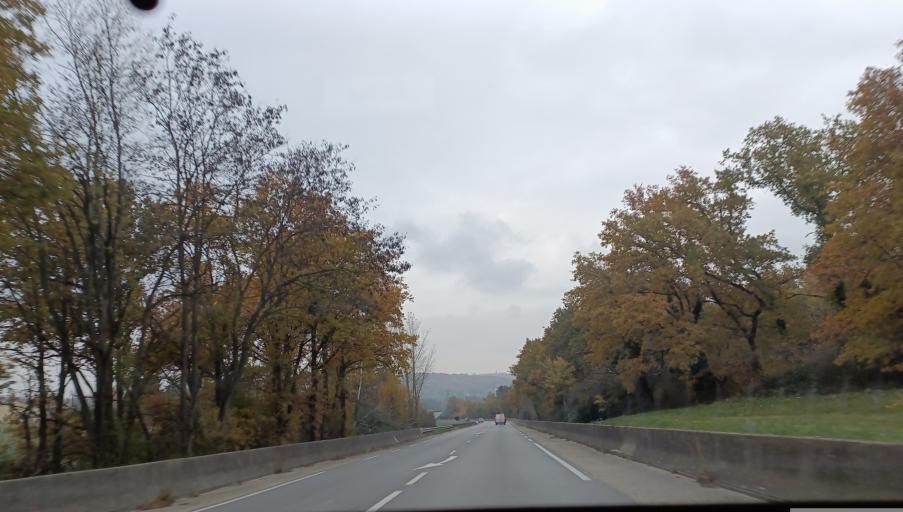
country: FR
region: Rhone-Alpes
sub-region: Departement de l'Isere
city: Pont-Eveque
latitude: 45.5293
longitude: 4.9295
